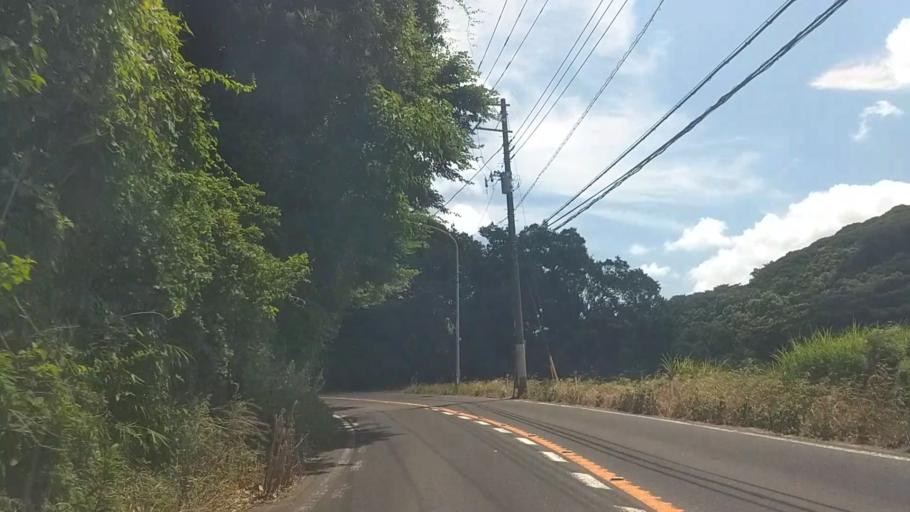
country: JP
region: Kanagawa
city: Miura
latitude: 35.2042
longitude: 139.6486
